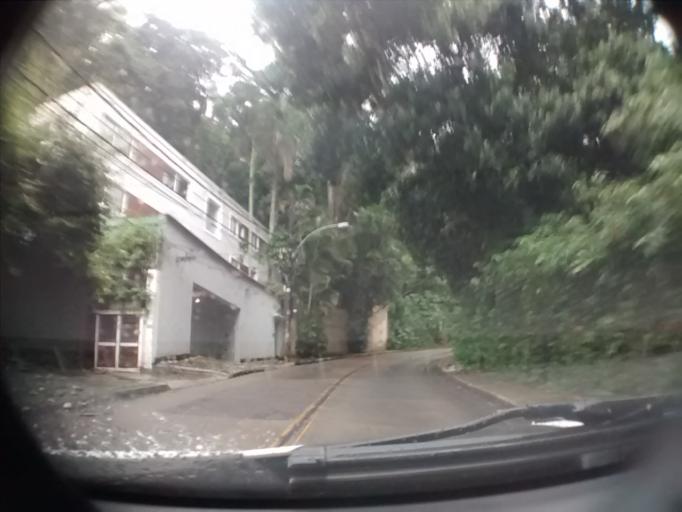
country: BR
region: Rio de Janeiro
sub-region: Rio De Janeiro
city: Rio de Janeiro
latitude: -22.9947
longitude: -43.2729
